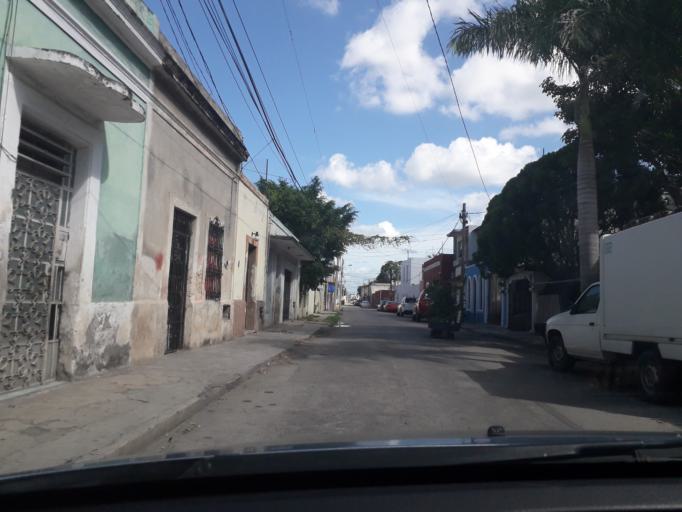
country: MX
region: Yucatan
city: Merida
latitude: 20.9588
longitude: -89.6229
